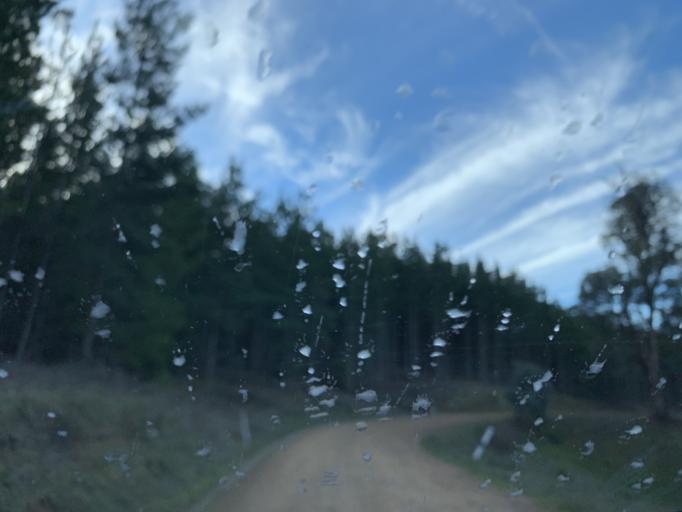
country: AU
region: Victoria
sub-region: Mansfield
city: Mansfield
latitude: -36.9251
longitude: 146.0992
